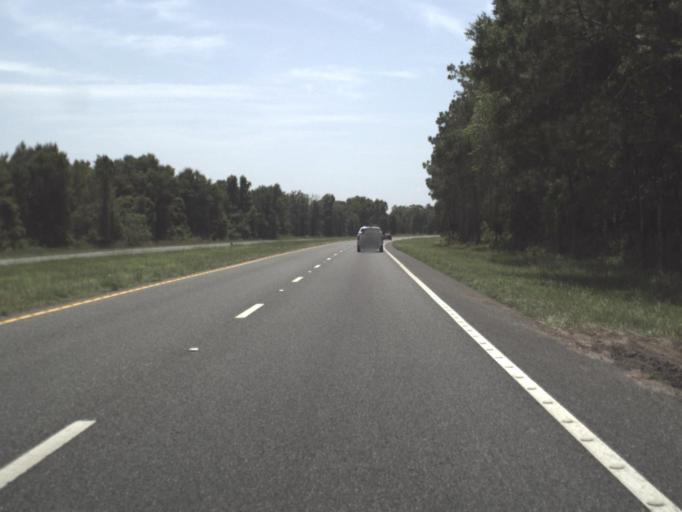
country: US
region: Florida
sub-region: Taylor County
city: Perry
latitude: 29.9488
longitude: -83.4549
